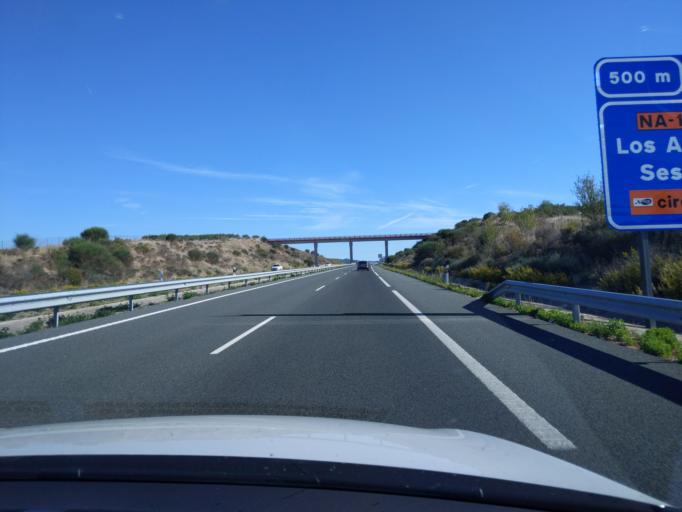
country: ES
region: Navarre
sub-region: Provincia de Navarra
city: Los Arcos
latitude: 42.5530
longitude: -2.1916
